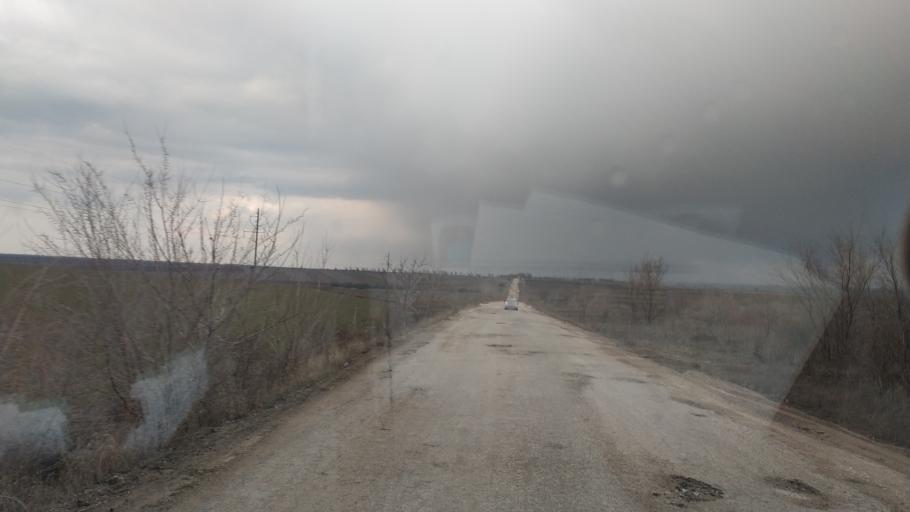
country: MD
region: Telenesti
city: Grigoriopol
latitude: 47.0568
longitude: 29.2949
